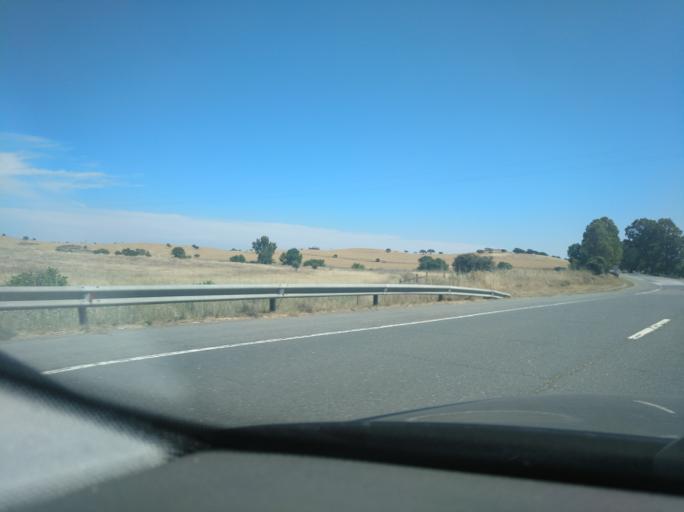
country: PT
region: Beja
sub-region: Castro Verde
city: Castro Verde
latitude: 37.6844
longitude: -8.0843
